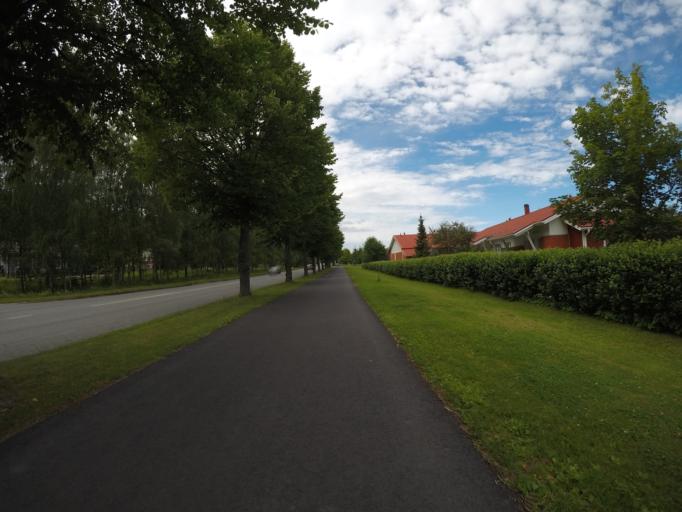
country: FI
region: Haeme
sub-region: Haemeenlinna
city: Haemeenlinna
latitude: 61.0076
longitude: 24.4086
